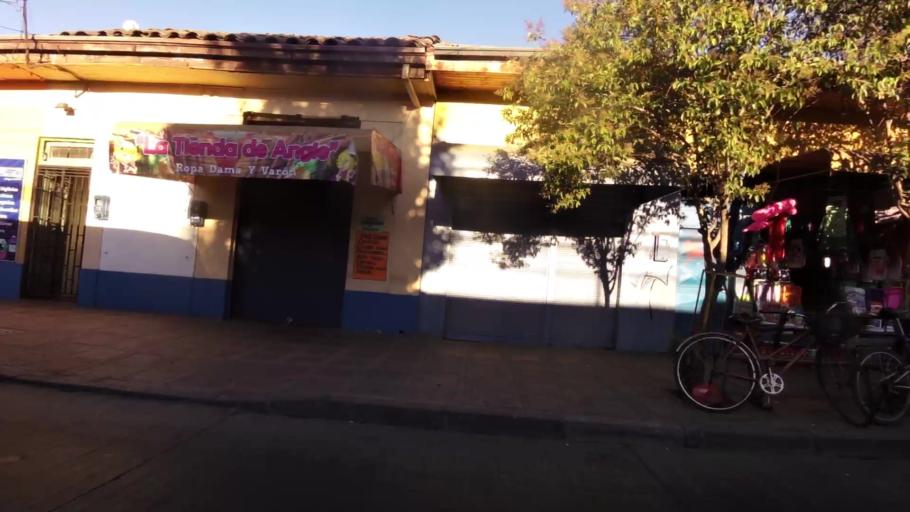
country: CL
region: Maule
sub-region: Provincia de Curico
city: Curico
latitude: -34.9838
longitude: -71.2444
